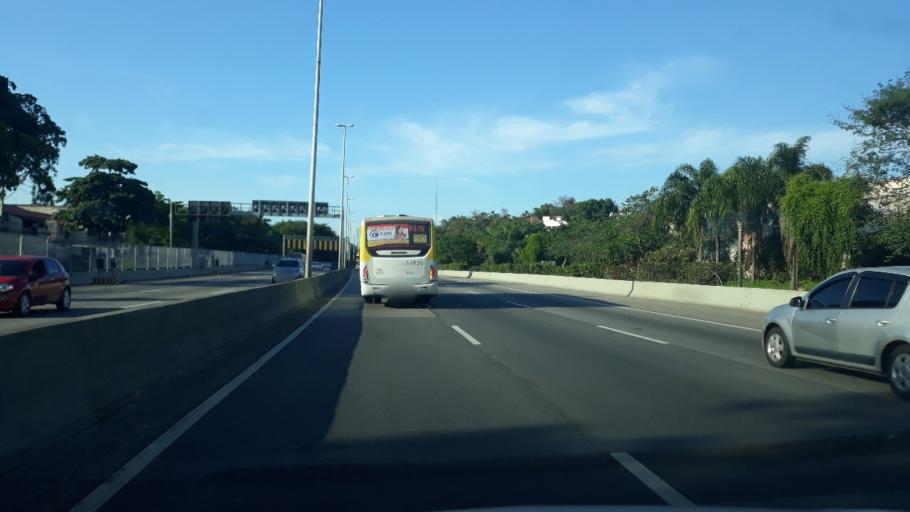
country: BR
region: Rio de Janeiro
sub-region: Sao Joao De Meriti
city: Sao Joao de Meriti
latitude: -22.9450
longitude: -43.3539
